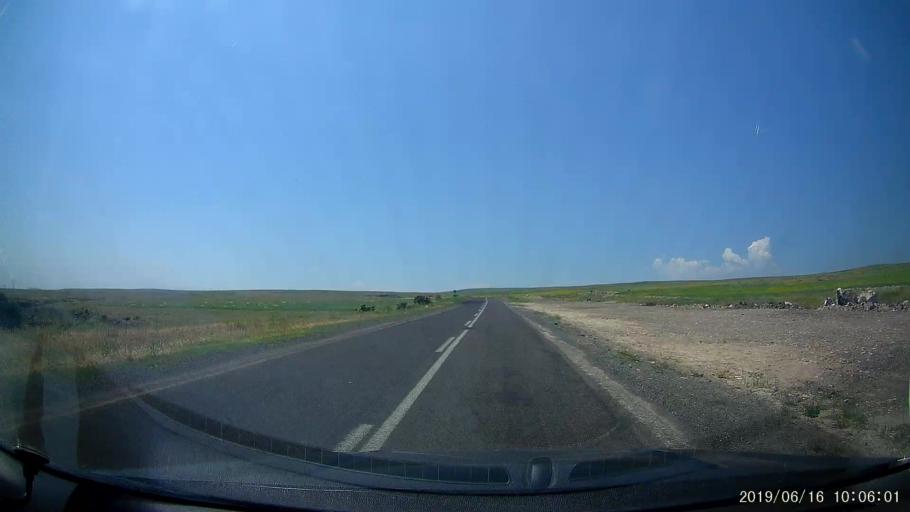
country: TR
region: Kars
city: Digor
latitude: 40.2618
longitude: 43.5403
